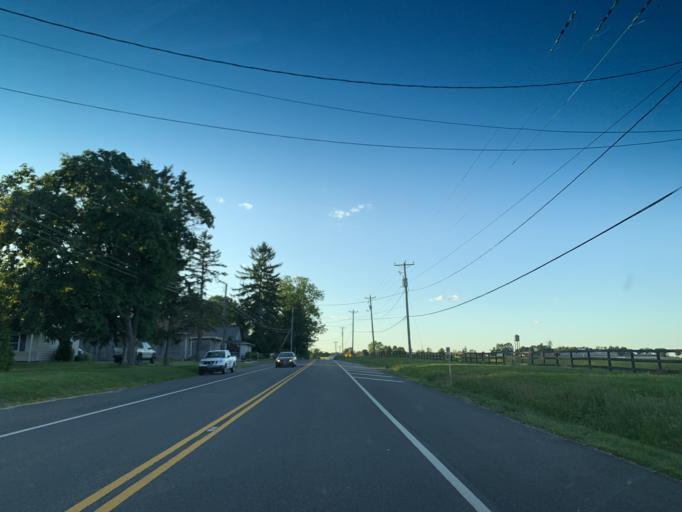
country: US
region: Maryland
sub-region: Cecil County
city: Elkton
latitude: 39.6940
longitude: -75.8675
